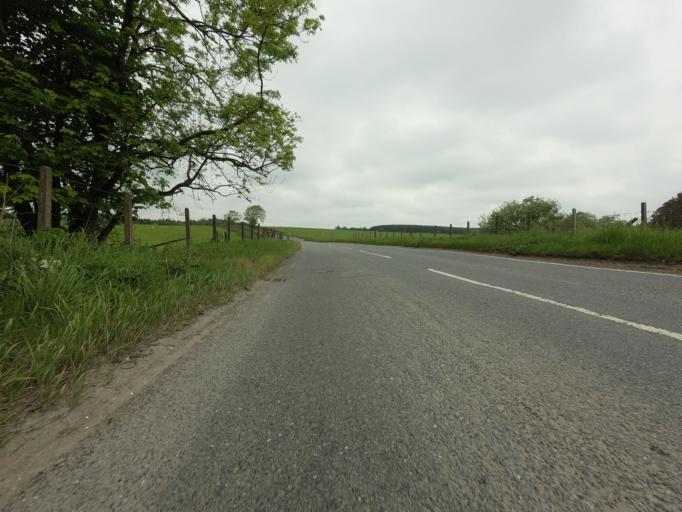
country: GB
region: Scotland
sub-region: Fife
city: Townhill
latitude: 56.1160
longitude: -3.4451
